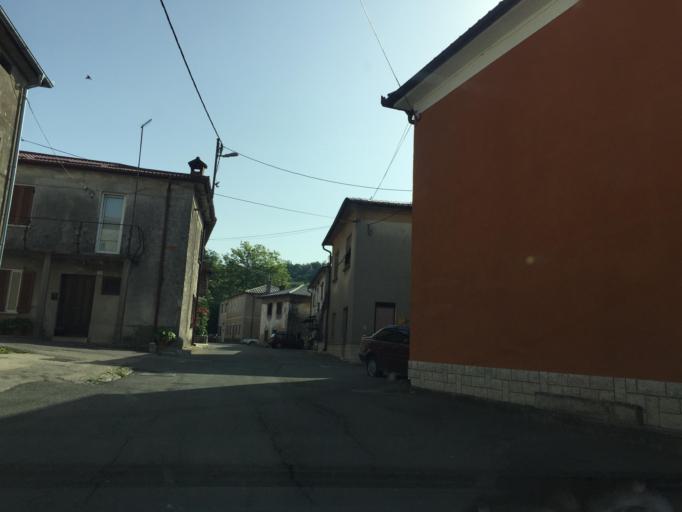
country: HR
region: Primorsko-Goranska
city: Klana
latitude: 45.4480
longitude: 14.3768
